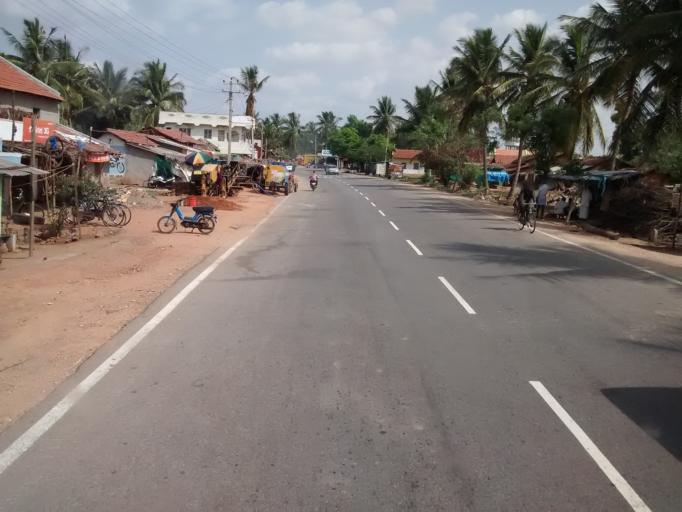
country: IN
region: Karnataka
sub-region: Mysore
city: Hunsur
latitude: 12.3671
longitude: 76.4178
